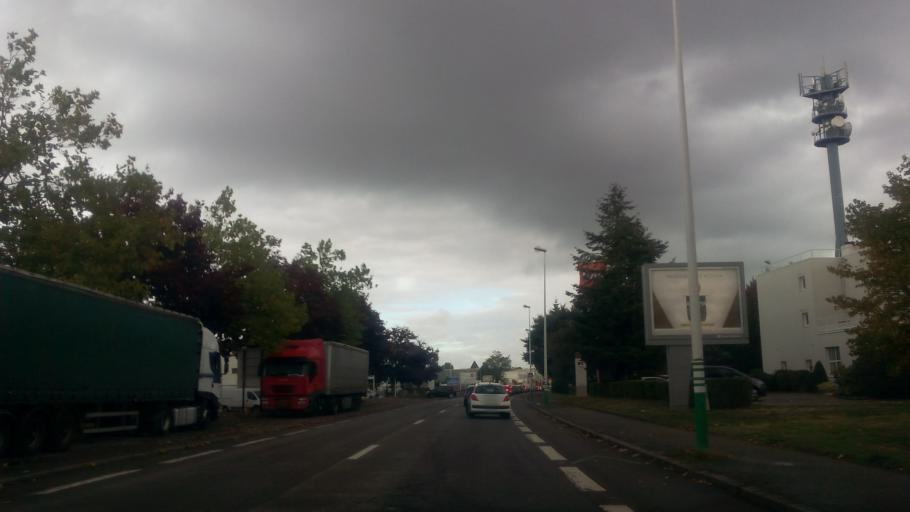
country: FR
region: Pays de la Loire
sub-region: Departement de la Loire-Atlantique
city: Saint-Herblain
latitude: 47.2242
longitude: -1.6388
